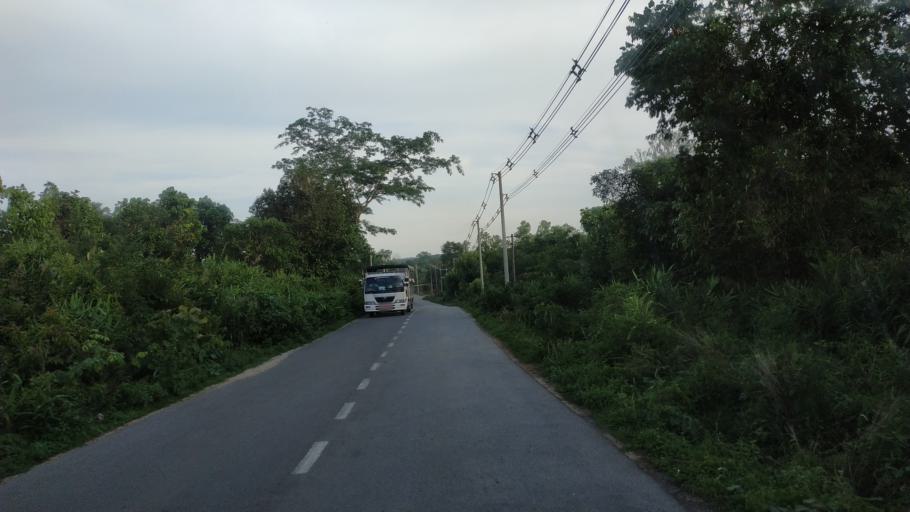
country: MM
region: Mon
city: Kyaikto
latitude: 17.4098
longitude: 97.0729
